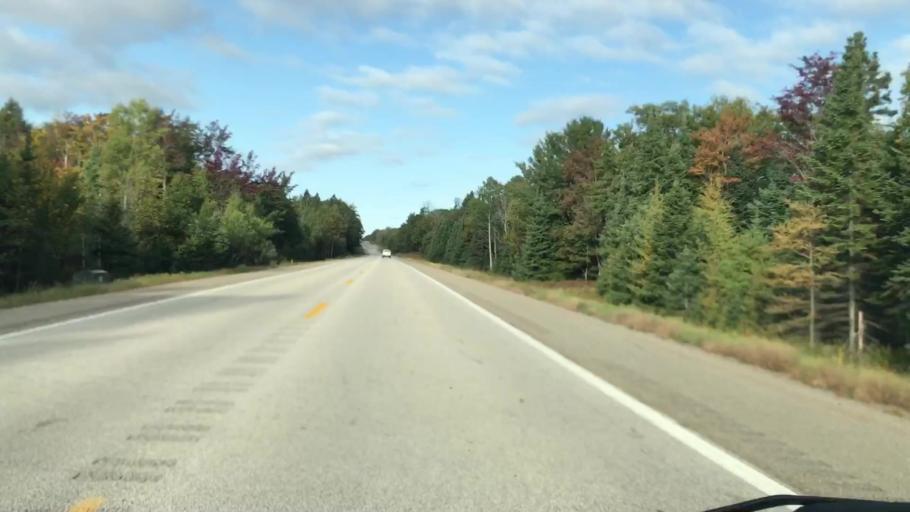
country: US
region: Michigan
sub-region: Luce County
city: Newberry
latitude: 46.3320
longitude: -85.0887
